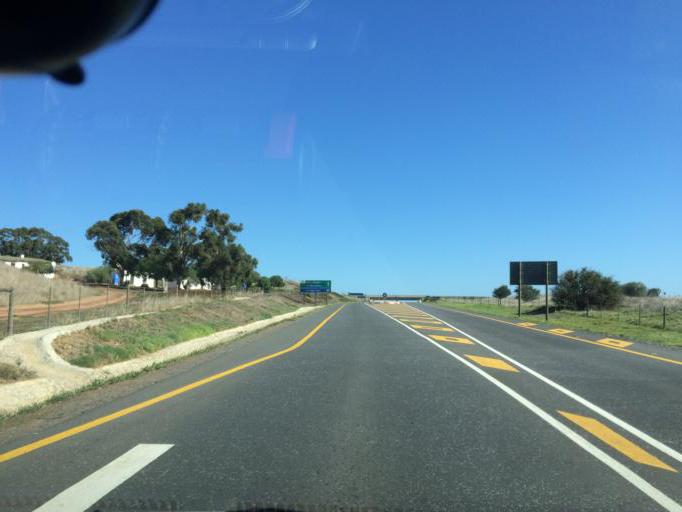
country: ZA
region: Western Cape
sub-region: City of Cape Town
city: Atlantis
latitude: -33.6650
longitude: 18.5634
